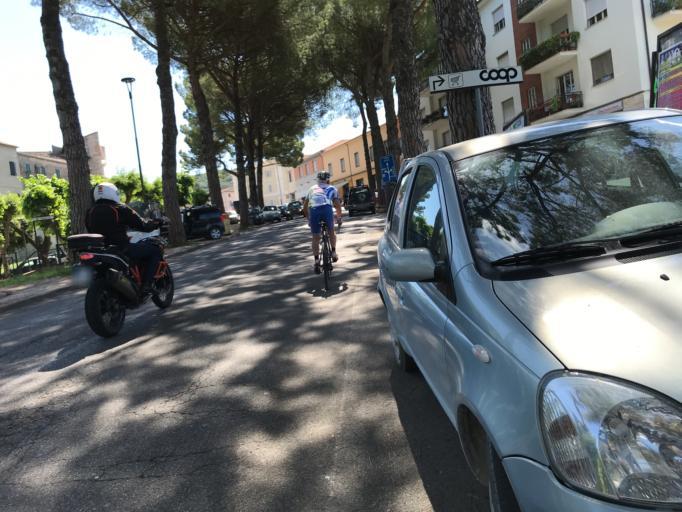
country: IT
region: Umbria
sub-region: Provincia di Terni
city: Amelia
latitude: 42.5536
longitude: 12.4154
